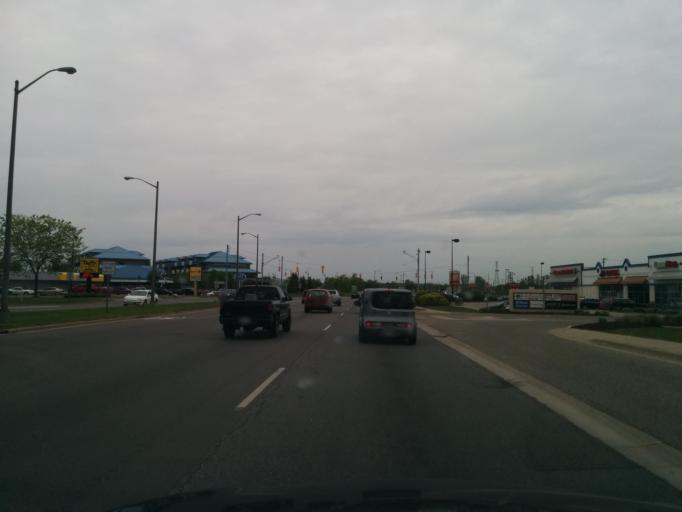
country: US
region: Michigan
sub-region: Ottawa County
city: Grand Haven
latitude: 43.0654
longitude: -86.2204
